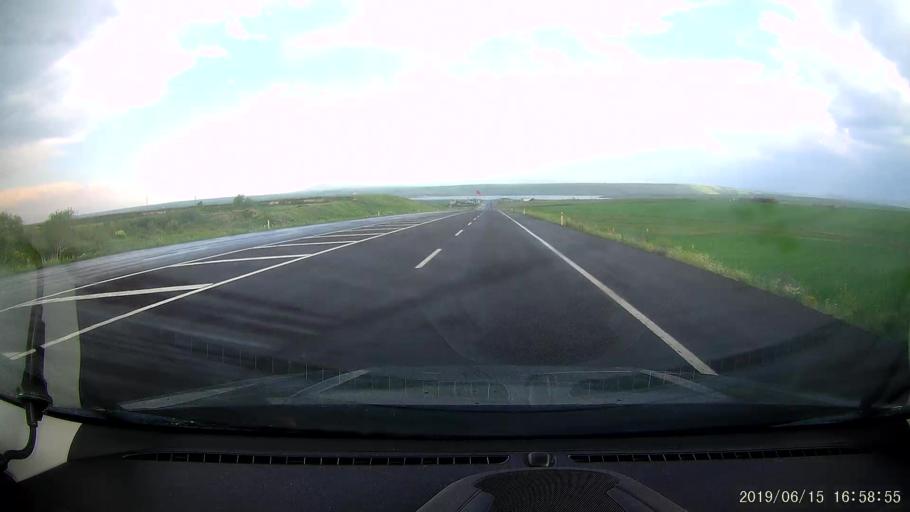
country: TR
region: Kars
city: Susuz
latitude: 40.7585
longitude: 43.1472
